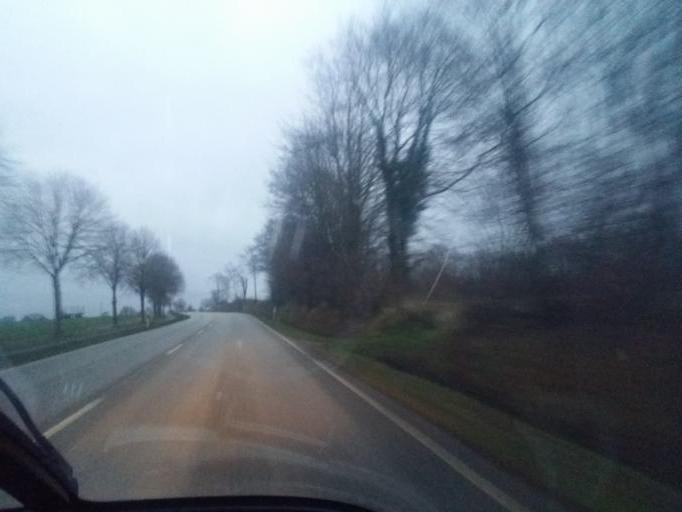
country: DE
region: Schleswig-Holstein
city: Gokels
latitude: 54.1166
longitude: 9.4553
